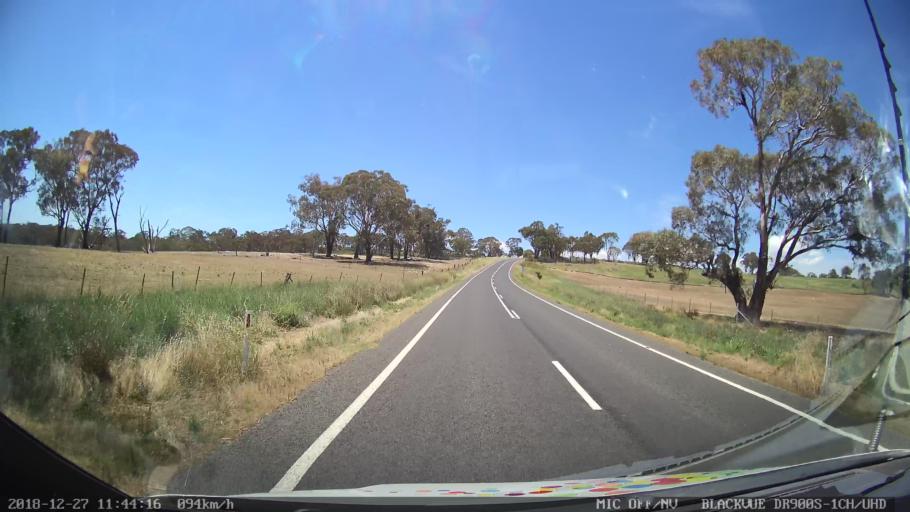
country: AU
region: New South Wales
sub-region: Bathurst Regional
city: Perthville
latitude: -33.5691
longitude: 149.4747
